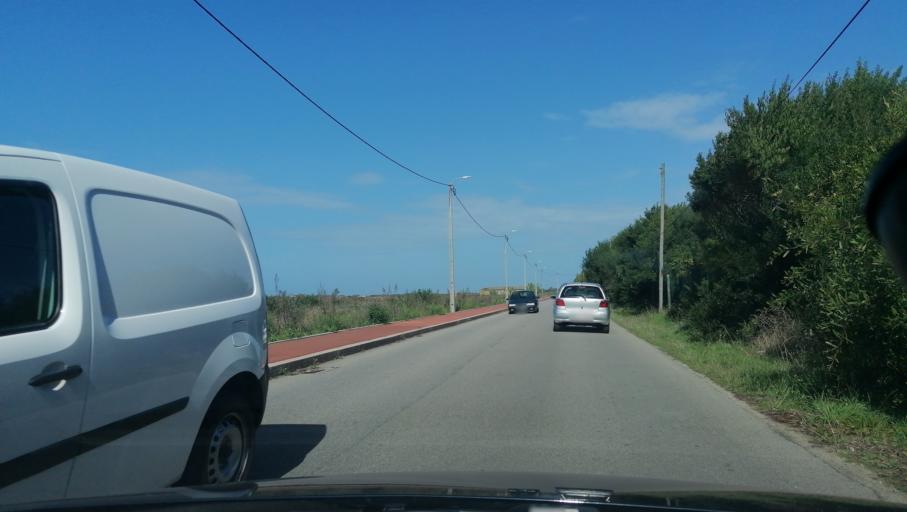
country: PT
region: Aveiro
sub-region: Espinho
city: Silvalde
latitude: 40.9850
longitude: -8.6431
